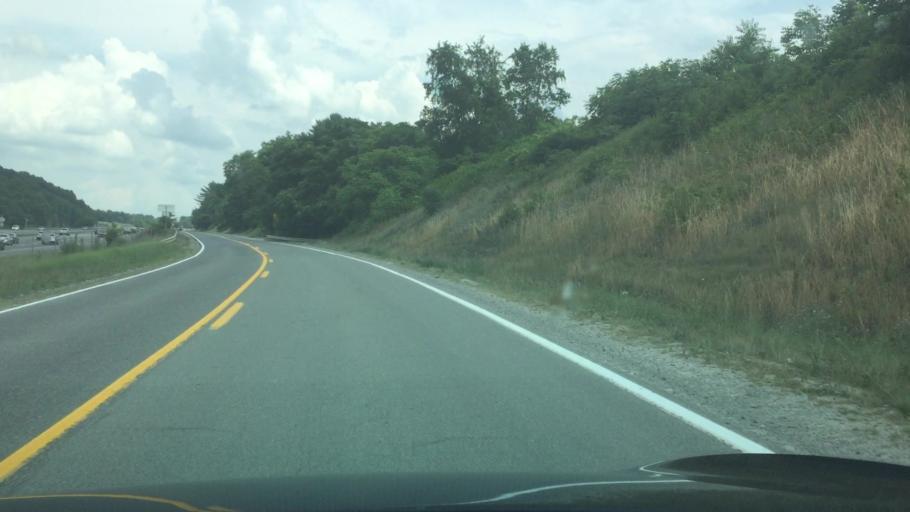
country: US
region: Virginia
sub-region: Wythe County
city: Wytheville
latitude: 36.9405
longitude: -81.0212
